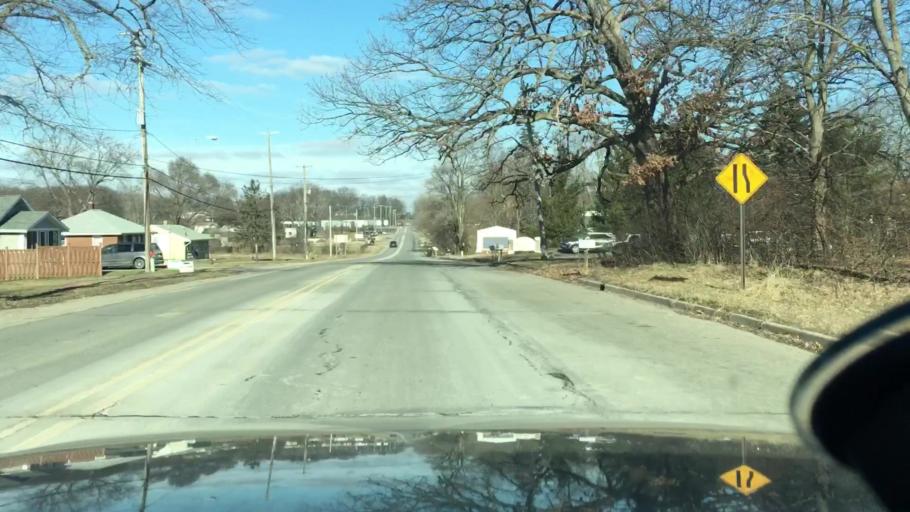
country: US
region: Michigan
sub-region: Jackson County
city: Jackson
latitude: 42.2804
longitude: -84.4299
